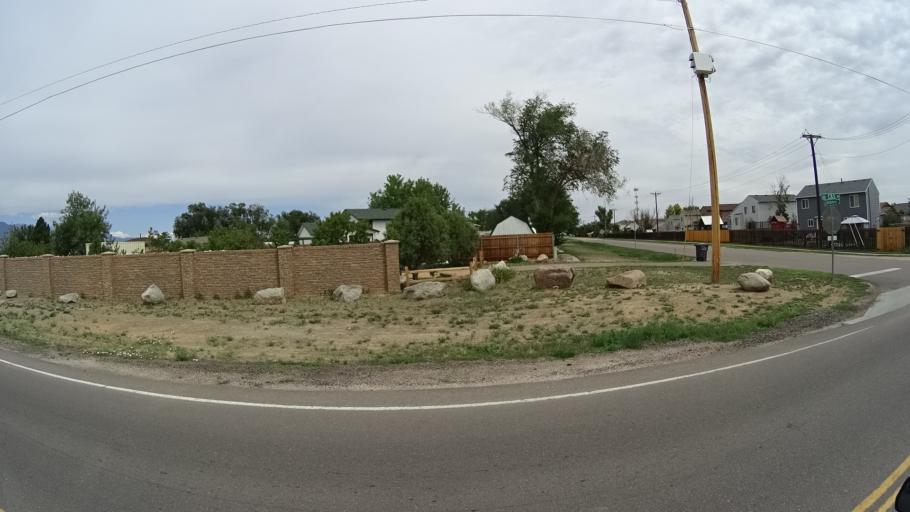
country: US
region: Colorado
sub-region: El Paso County
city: Fountain
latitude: 38.7083
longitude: -104.7015
